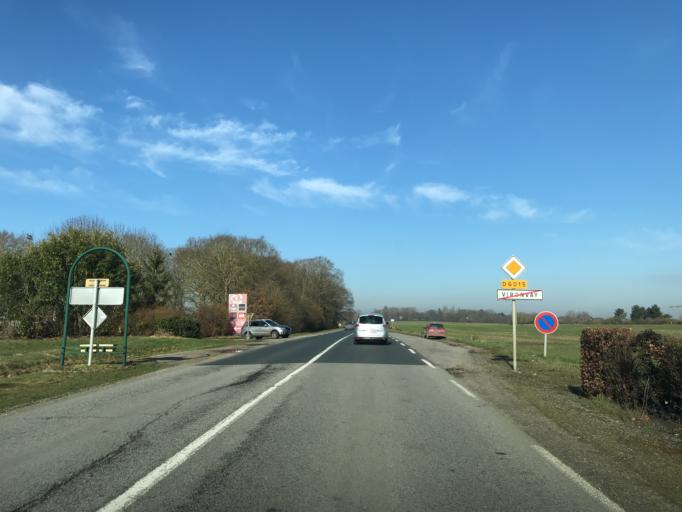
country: FR
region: Haute-Normandie
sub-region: Departement de l'Eure
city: Saint-Pierre-du-Vauvray
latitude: 49.2105
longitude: 1.2230
